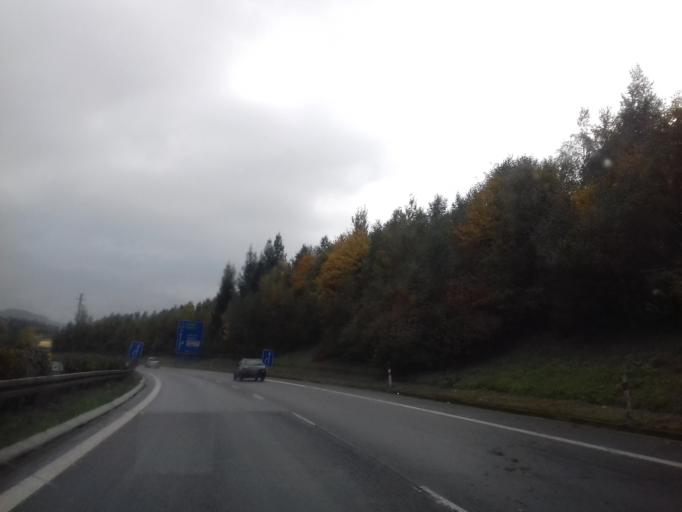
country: CZ
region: Liberecky
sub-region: Okres Liberec
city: Liberec
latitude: 50.7349
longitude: 15.0483
